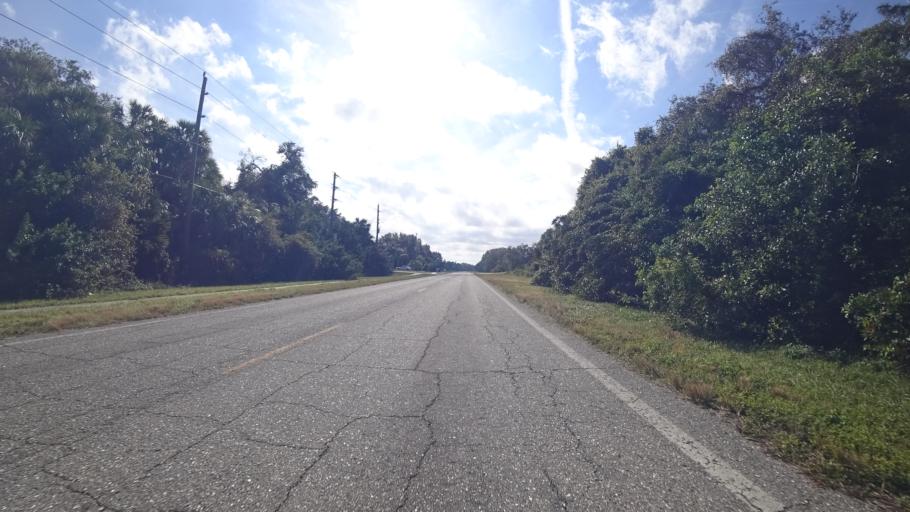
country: US
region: Florida
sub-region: Charlotte County
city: Port Charlotte
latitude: 27.0608
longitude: -82.1164
